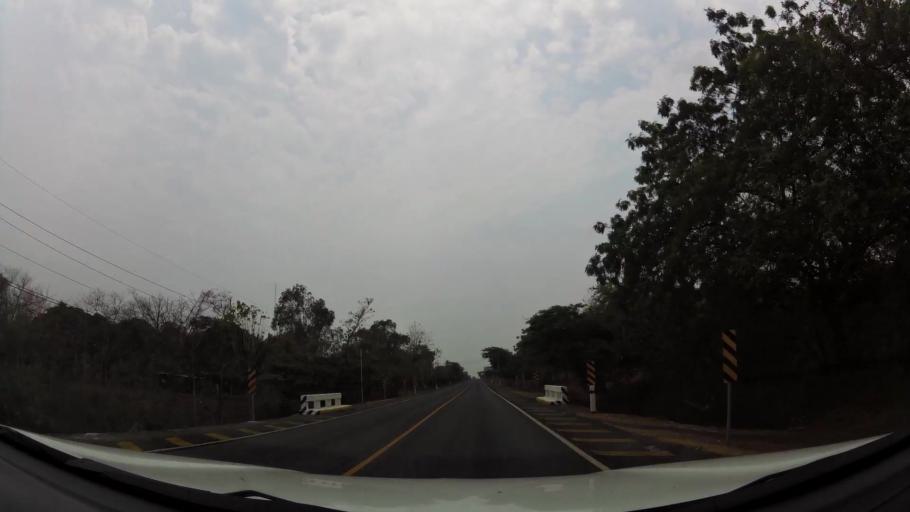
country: NI
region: Chinandega
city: Chichigalpa
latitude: 12.6040
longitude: -87.0527
